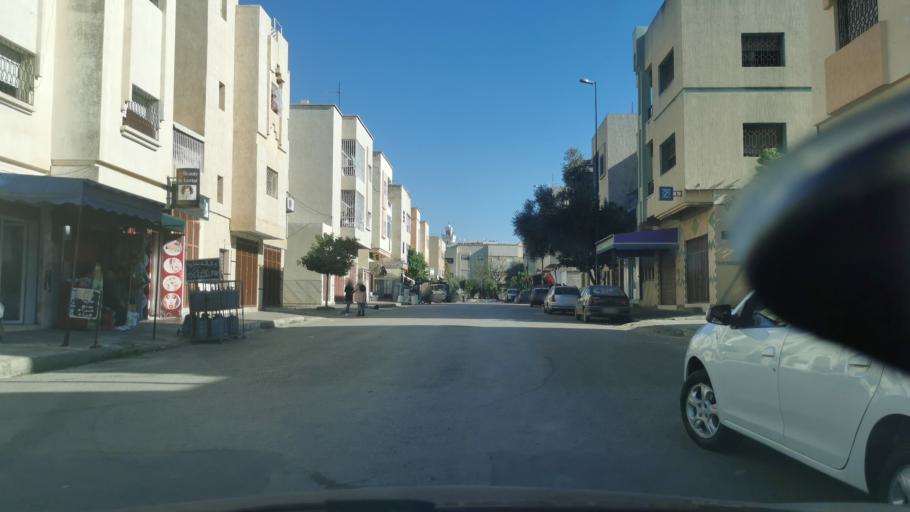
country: MA
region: Fes-Boulemane
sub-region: Fes
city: Fes
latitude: 34.0154
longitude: -4.9796
